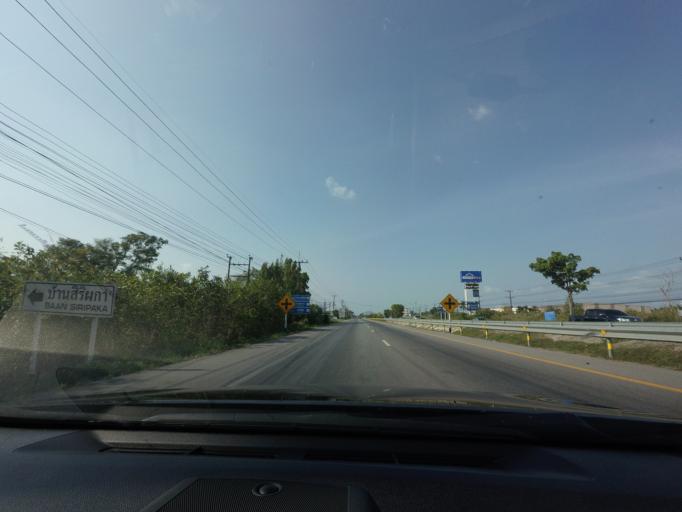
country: TH
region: Prachuap Khiri Khan
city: Prachuap Khiri Khan
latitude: 11.7900
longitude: 99.7740
